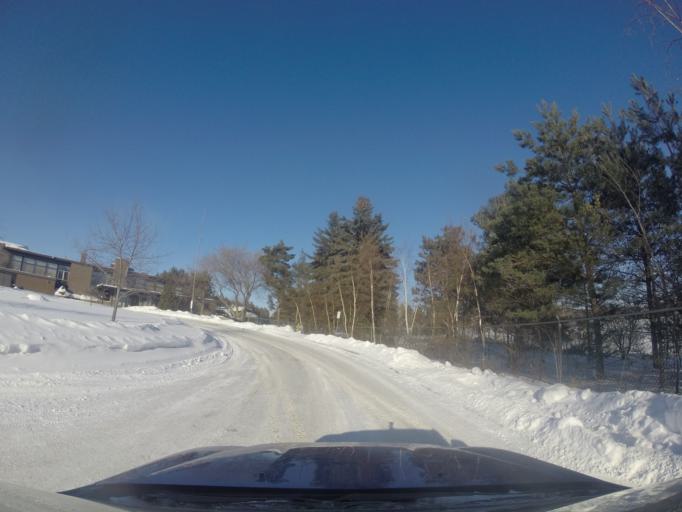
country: CA
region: Ontario
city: Greater Sudbury
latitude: 46.4642
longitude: -80.9865
